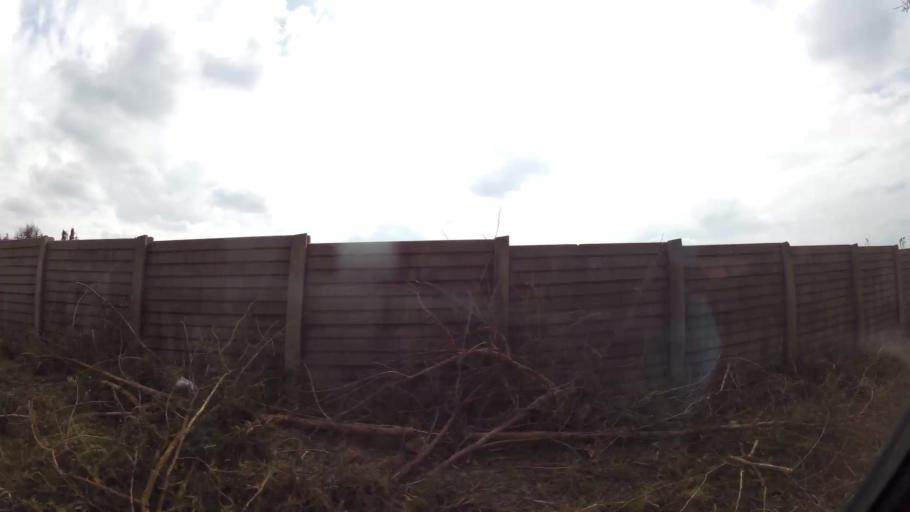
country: ZA
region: Gauteng
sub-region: City of Johannesburg Metropolitan Municipality
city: Roodepoort
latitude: -26.1011
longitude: 27.8844
